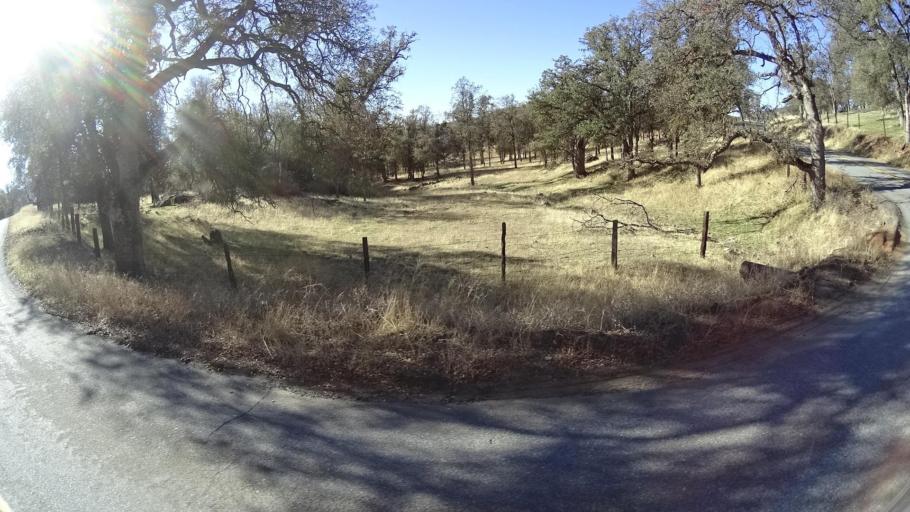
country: US
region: California
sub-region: Kern County
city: Alta Sierra
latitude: 35.7983
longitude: -118.7131
